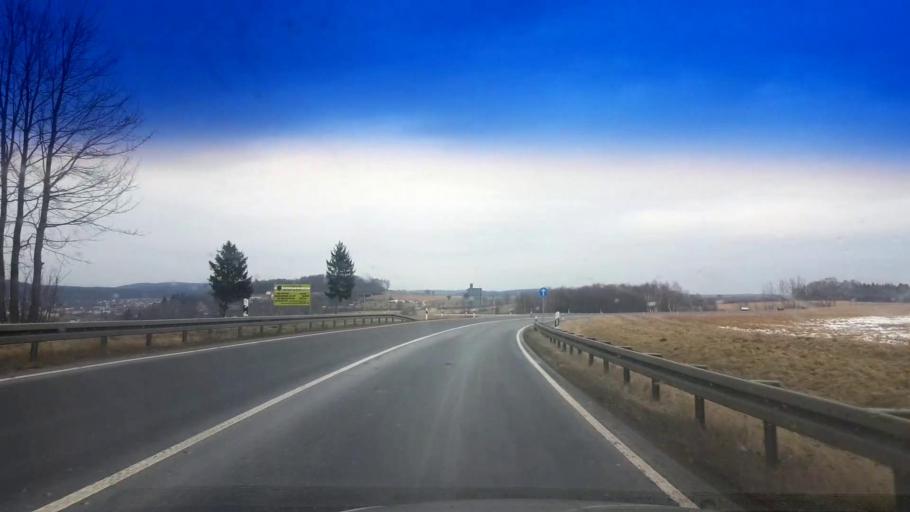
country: DE
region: Bavaria
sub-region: Upper Franconia
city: Wunsiedel
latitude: 50.0232
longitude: 11.9985
